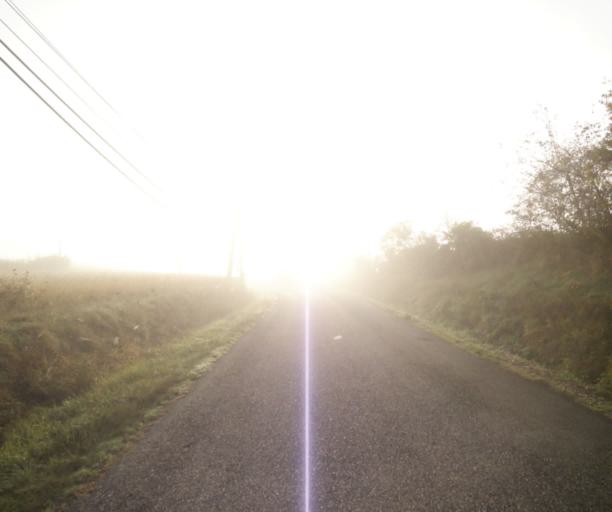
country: FR
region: Midi-Pyrenees
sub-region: Departement du Tarn-et-Garonne
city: Nohic
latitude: 43.9053
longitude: 1.4628
